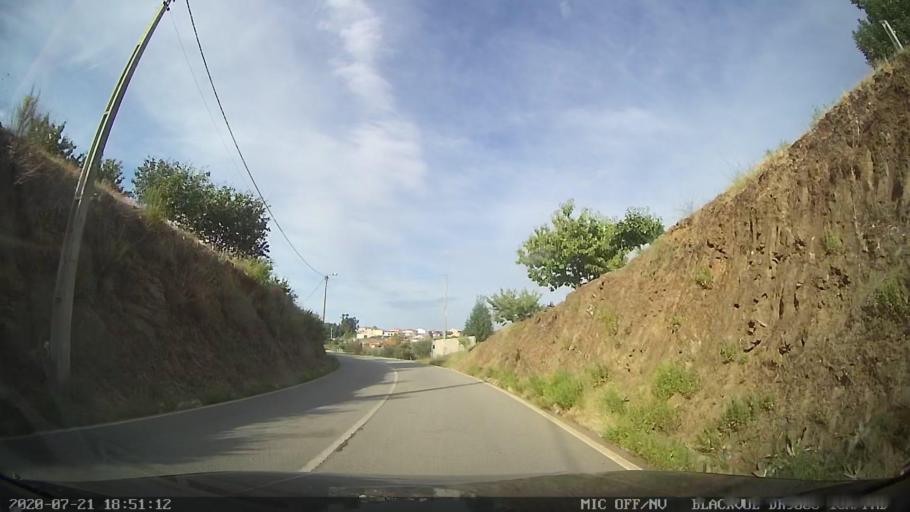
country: PT
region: Viseu
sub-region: Sao Joao da Pesqueira
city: Sao Joao da Pesqueira
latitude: 41.1426
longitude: -7.4243
